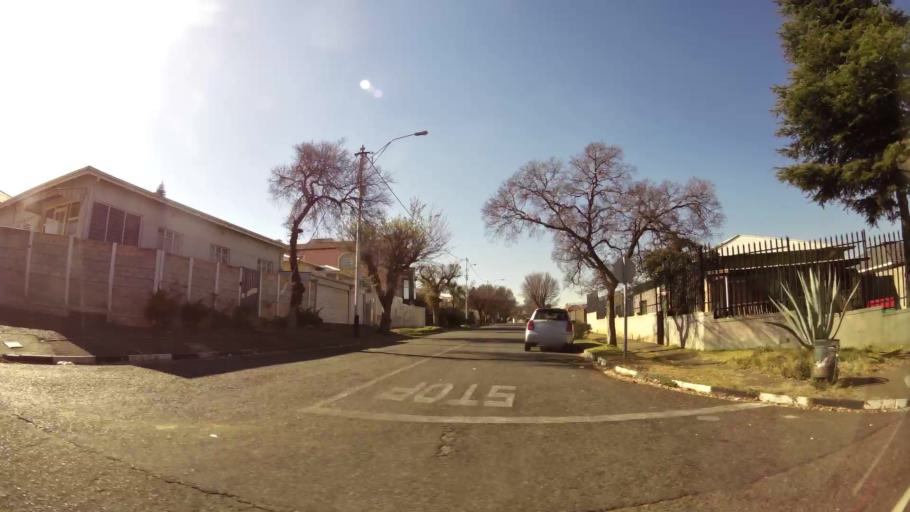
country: ZA
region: Gauteng
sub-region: City of Johannesburg Metropolitan Municipality
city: Johannesburg
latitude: -26.1984
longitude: 27.9937
